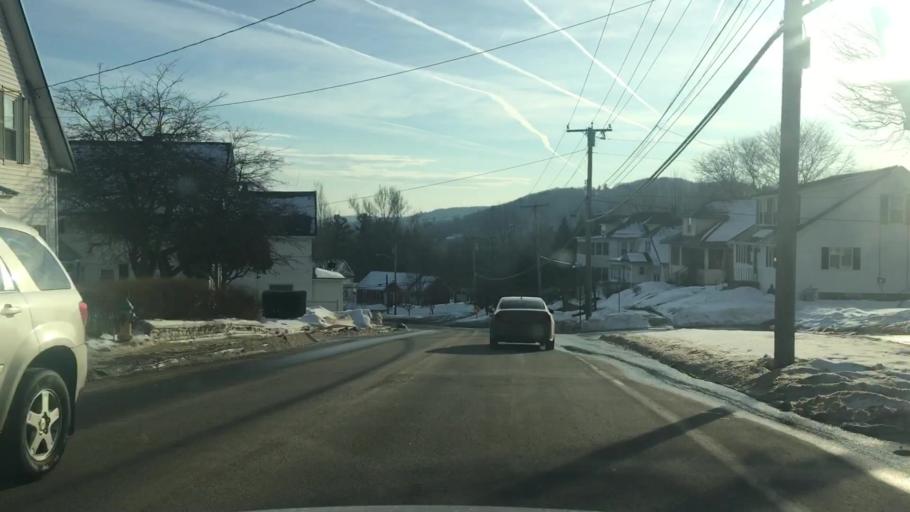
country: US
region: Maine
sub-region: Kennebec County
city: Augusta
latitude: 44.3292
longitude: -69.7770
